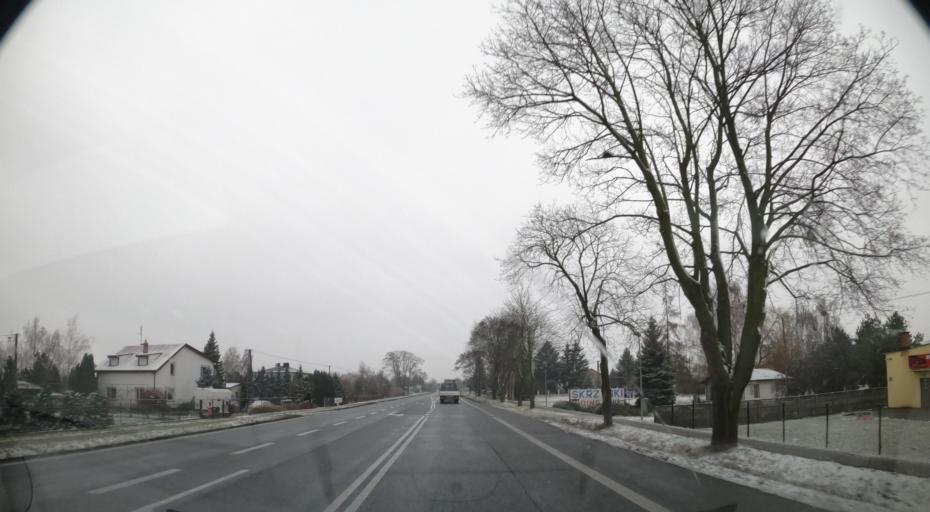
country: PL
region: Masovian Voivodeship
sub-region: Powiat sochaczewski
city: Paprotnia
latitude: 52.2128
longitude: 20.4207
